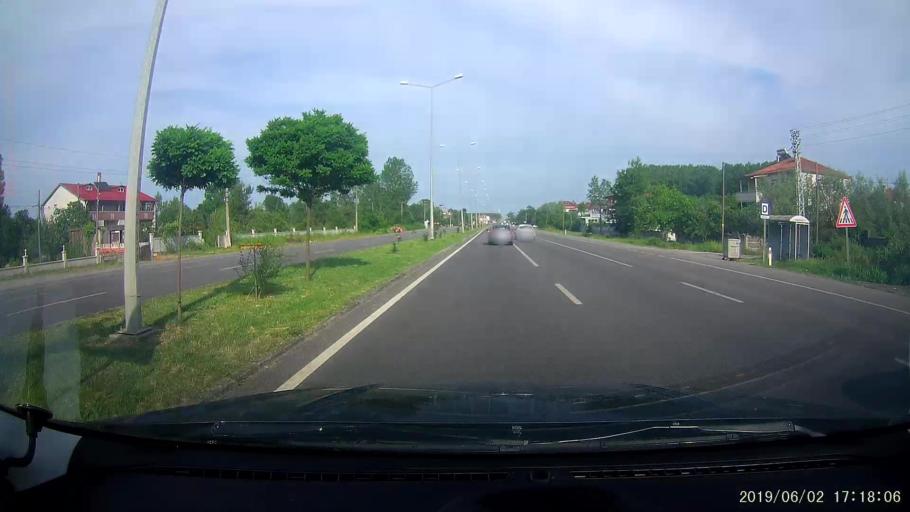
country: TR
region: Samsun
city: Dikbiyik
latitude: 41.2253
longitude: 36.5923
